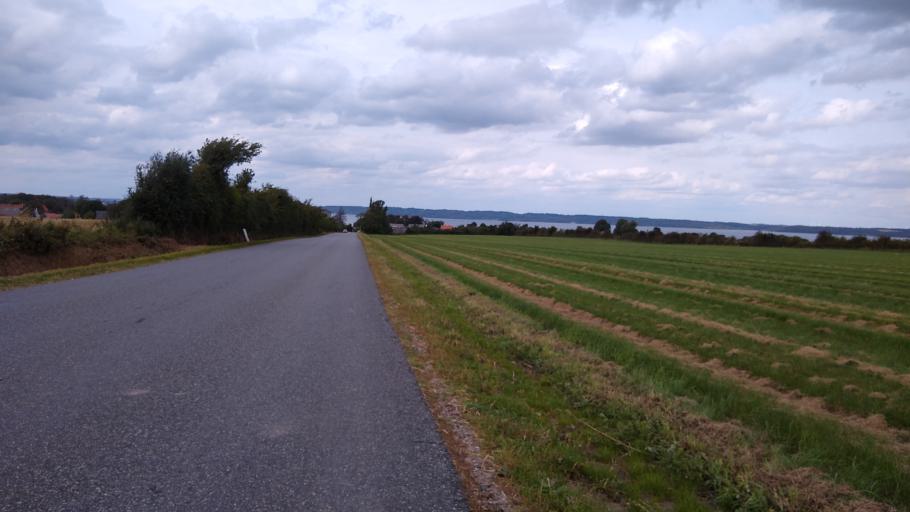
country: DK
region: South Denmark
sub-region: Fredericia Kommune
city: Fredericia
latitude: 55.6140
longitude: 9.7780
